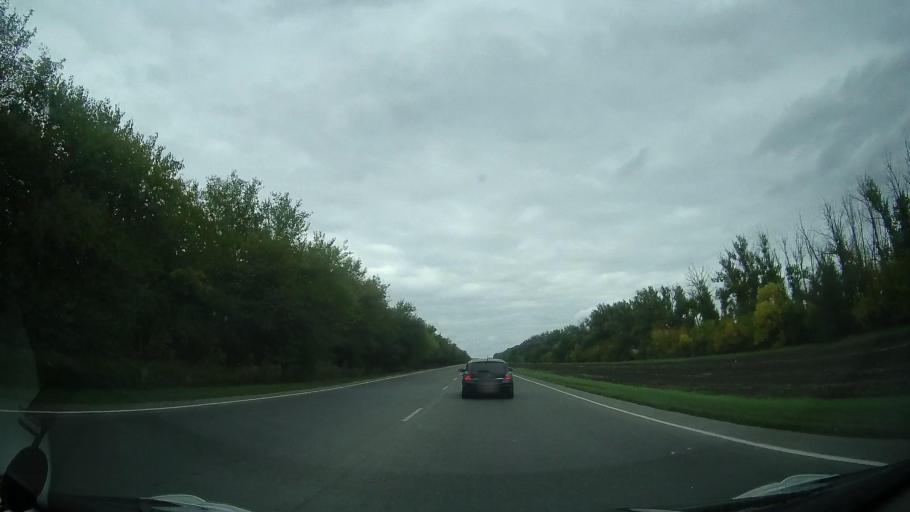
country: RU
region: Rostov
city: Yegorlykskaya
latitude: 46.6060
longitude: 40.6125
